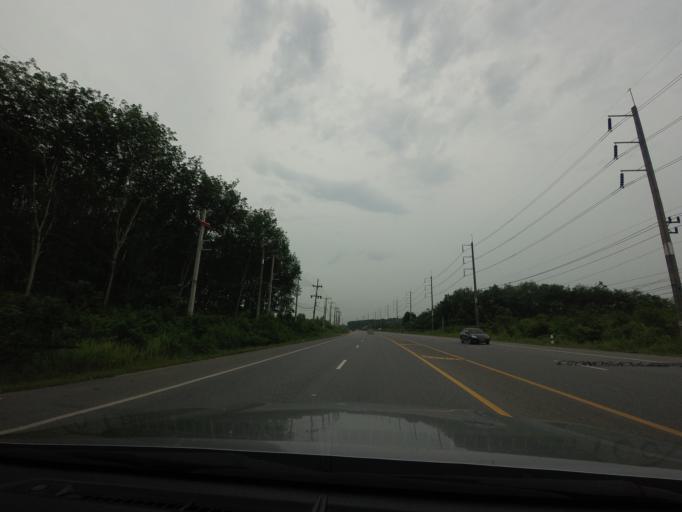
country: TH
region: Songkhla
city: Na Mom
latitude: 7.0241
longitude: 100.6653
